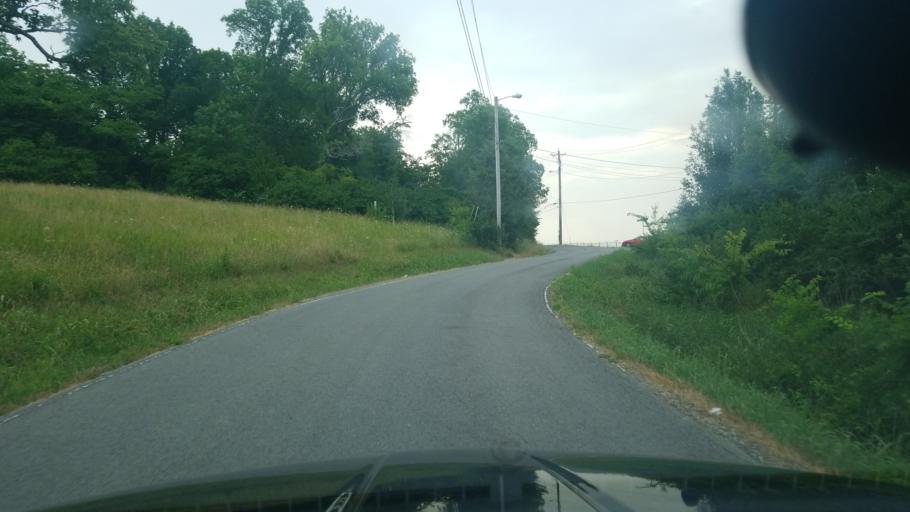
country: US
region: Tennessee
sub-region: Davidson County
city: Goodlettsville
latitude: 36.2490
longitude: -86.7492
